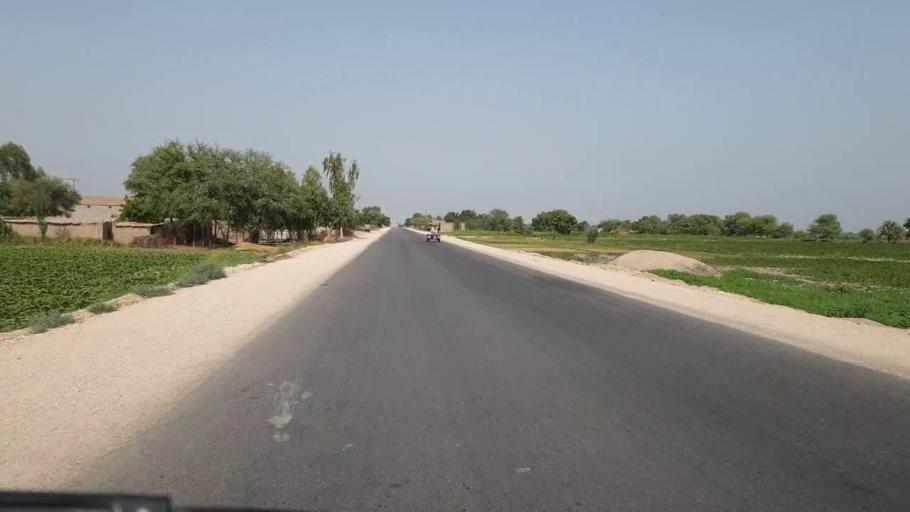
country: PK
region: Sindh
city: Sakrand
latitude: 26.2450
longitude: 68.2505
